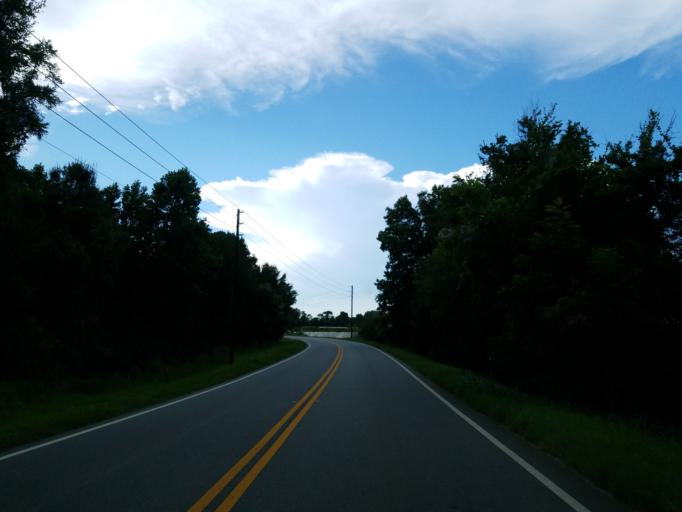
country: US
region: Georgia
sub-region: Tift County
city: Unionville
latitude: 31.4046
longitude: -83.4960
